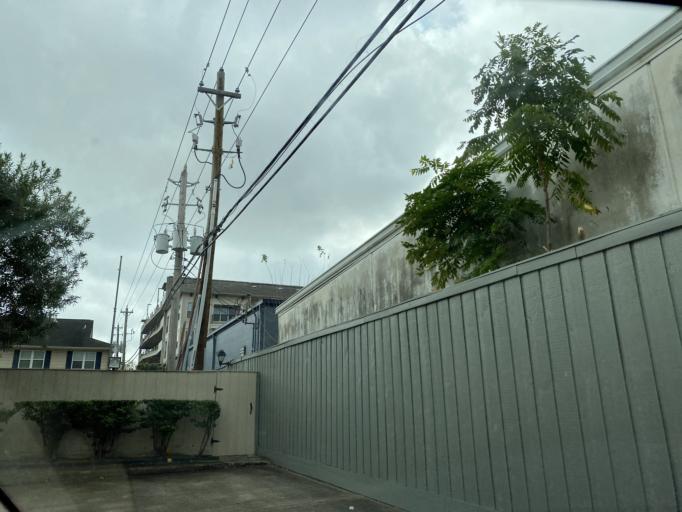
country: US
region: Texas
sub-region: Harris County
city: Piney Point Village
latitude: 29.7438
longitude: -95.4994
